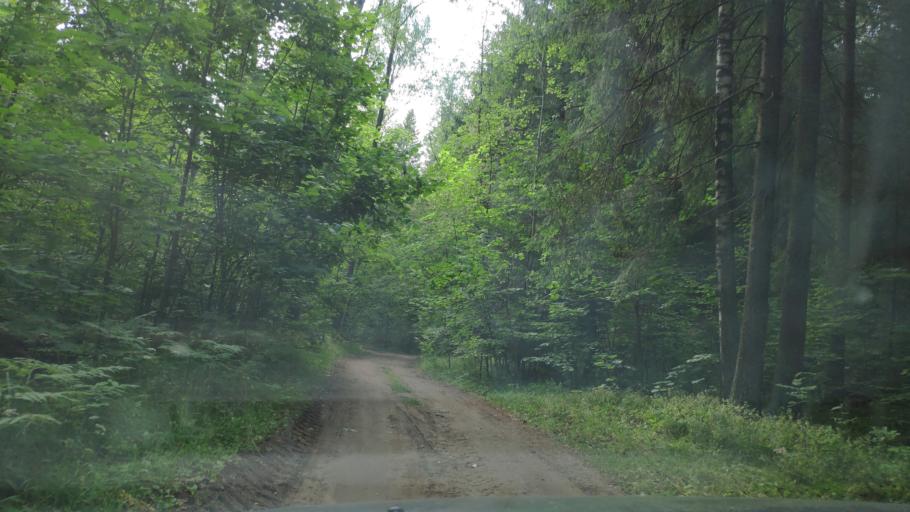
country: BY
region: Minsk
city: Zaslawye
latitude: 53.9643
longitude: 27.2974
